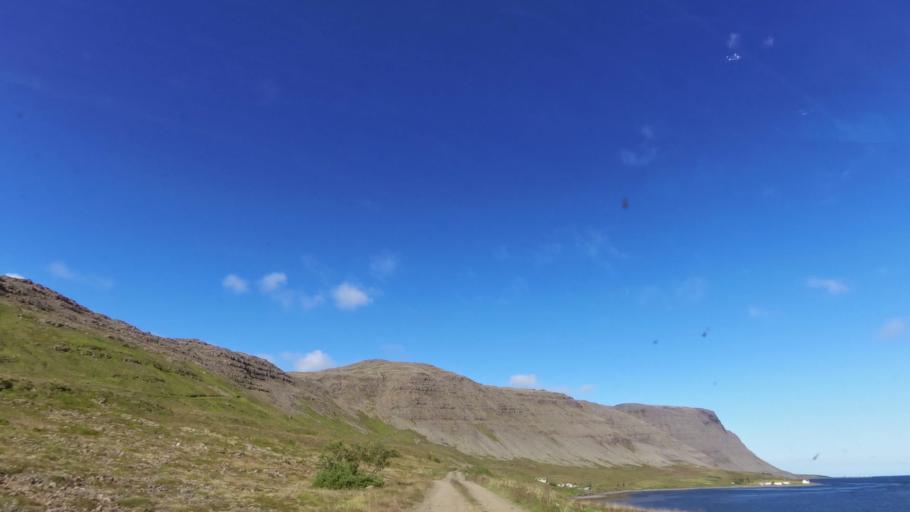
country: IS
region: West
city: Olafsvik
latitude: 65.6170
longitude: -23.8490
